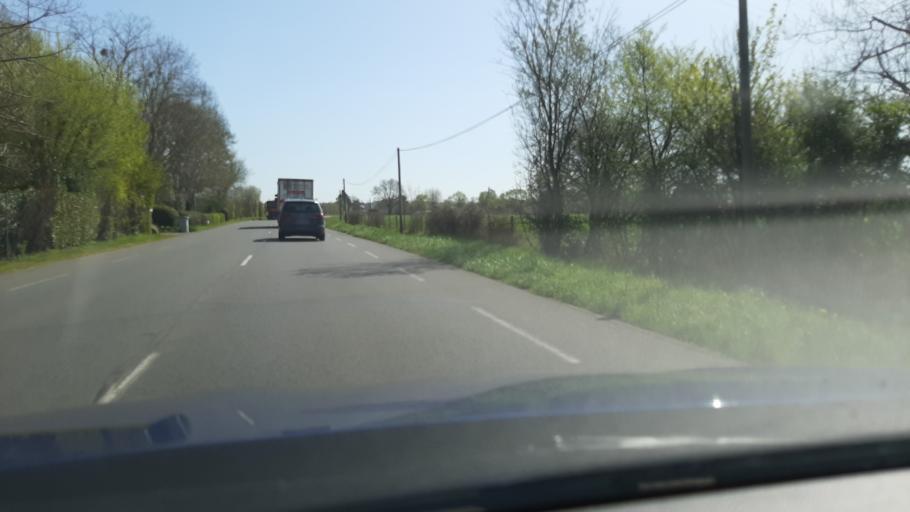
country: FR
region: Pays de la Loire
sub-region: Departement de Maine-et-Loire
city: Ecouflant
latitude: 47.5195
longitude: -0.4874
